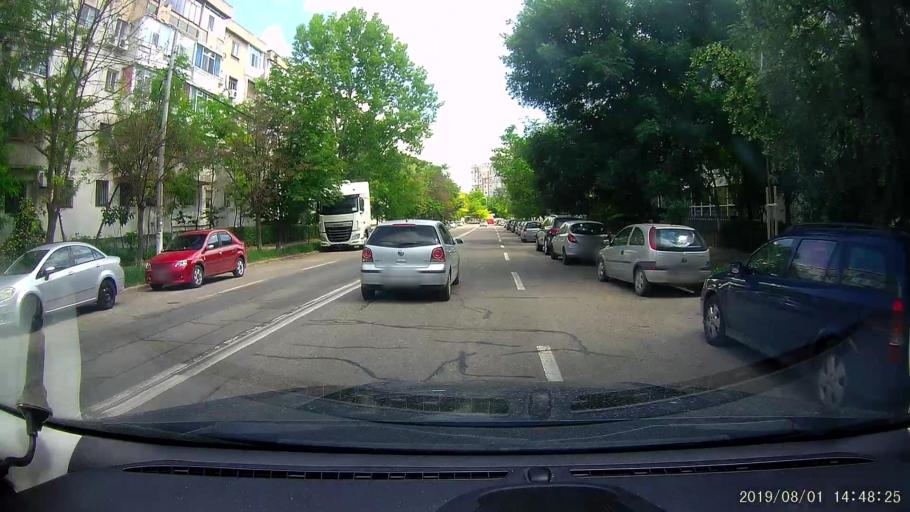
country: RO
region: Galati
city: Galati
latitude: 45.4108
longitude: 28.0089
